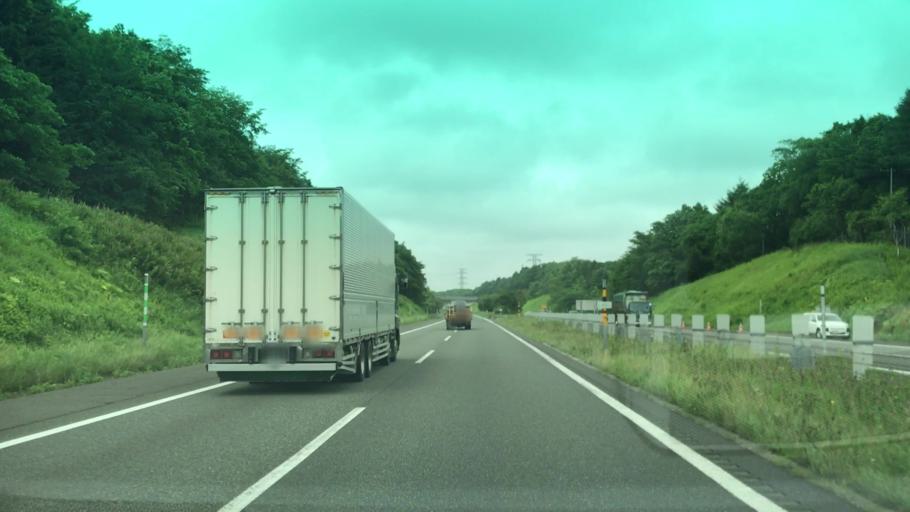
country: JP
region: Hokkaido
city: Chitose
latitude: 42.7277
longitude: 141.6530
